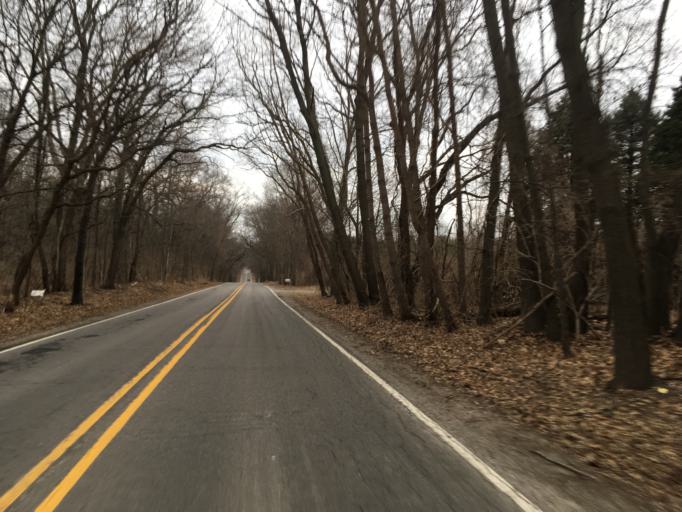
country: US
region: Michigan
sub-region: Washtenaw County
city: Chelsea
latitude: 42.3537
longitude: -84.1205
